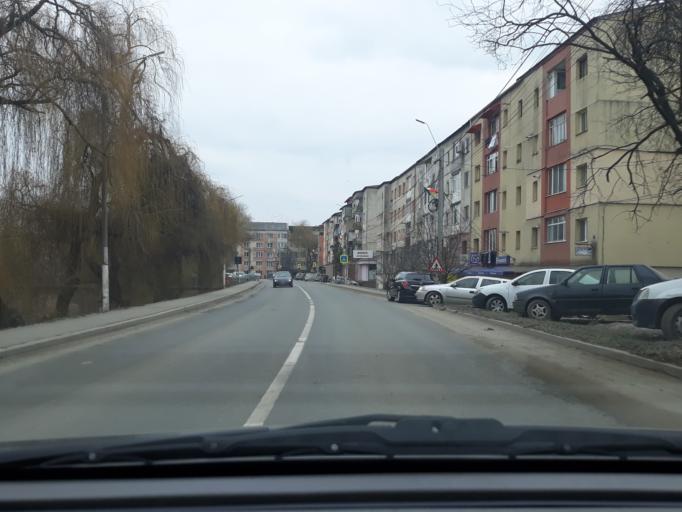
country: RO
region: Salaj
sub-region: Oras Simleu Silvaniei
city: Simleu Silvaniei
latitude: 47.2270
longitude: 22.7913
